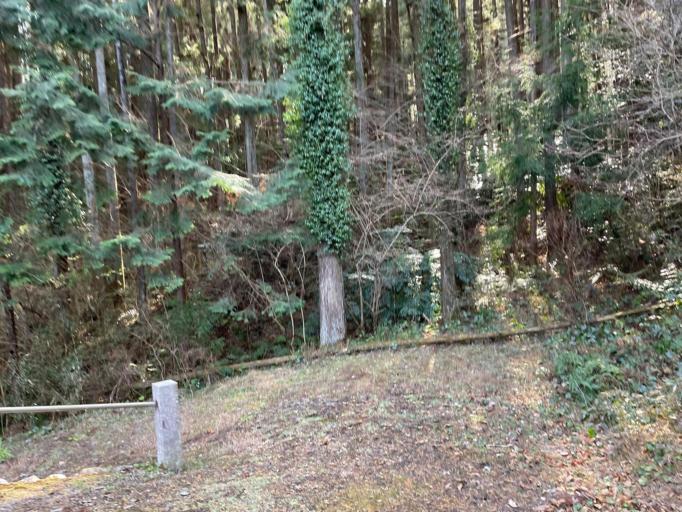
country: JP
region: Saitama
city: Hanno
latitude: 35.8417
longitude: 139.2740
